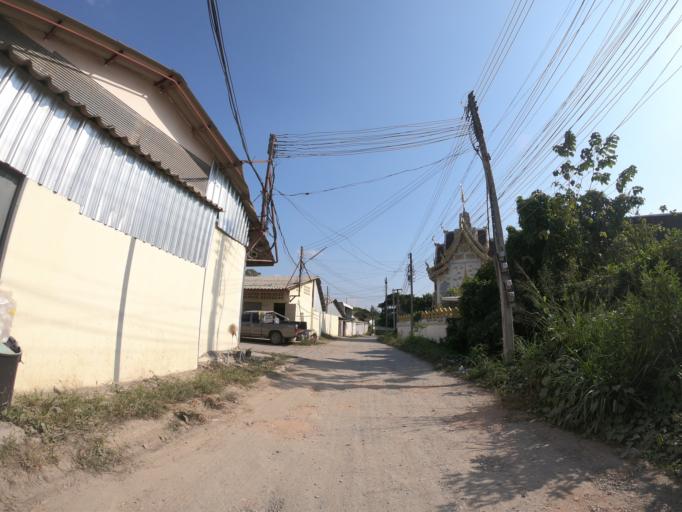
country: TH
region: Chiang Mai
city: Chiang Mai
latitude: 18.8184
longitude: 99.0041
